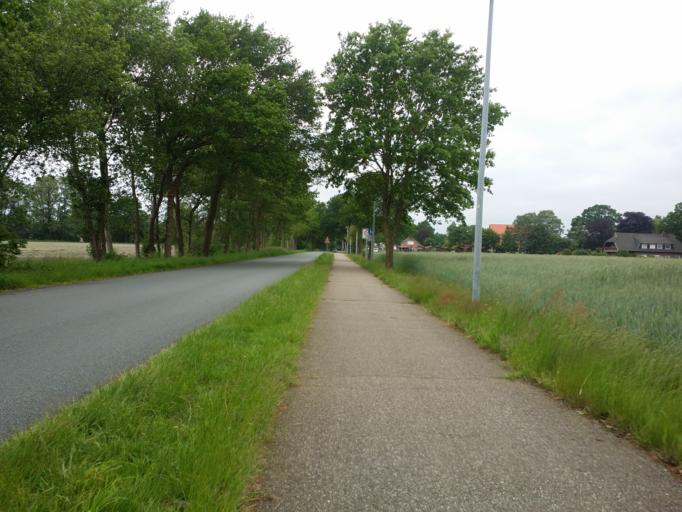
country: DE
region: Lower Saxony
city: Hatten
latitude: 53.1145
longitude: 8.3486
